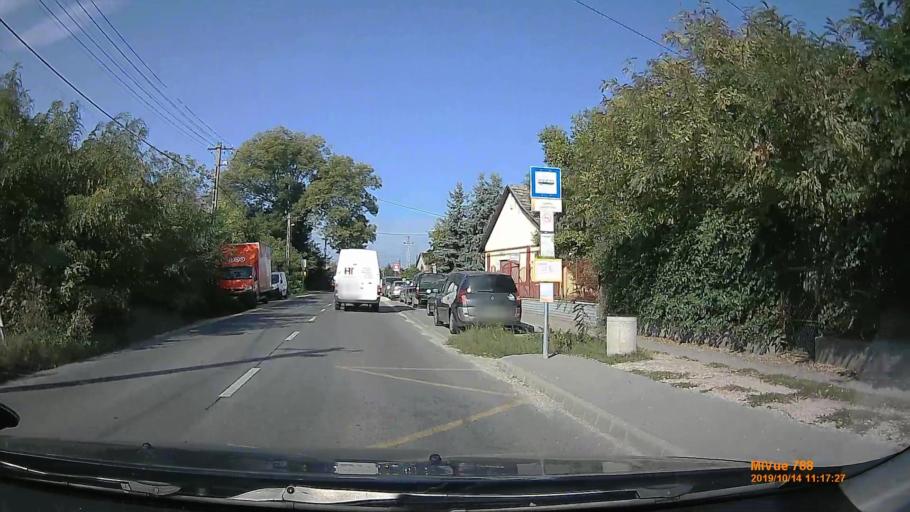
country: HU
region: Pest
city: Gyomro
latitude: 47.4165
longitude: 19.3933
